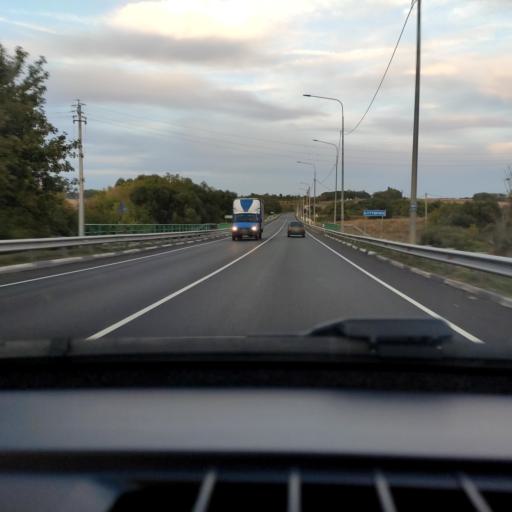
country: RU
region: Voronezj
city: Panino
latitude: 51.4859
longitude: 40.2018
